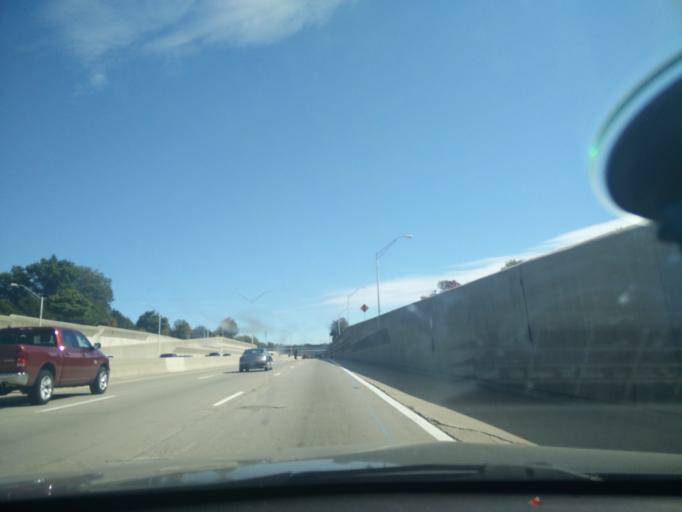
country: US
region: Michigan
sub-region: Oakland County
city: Lathrup Village
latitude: 42.4870
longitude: -83.2485
